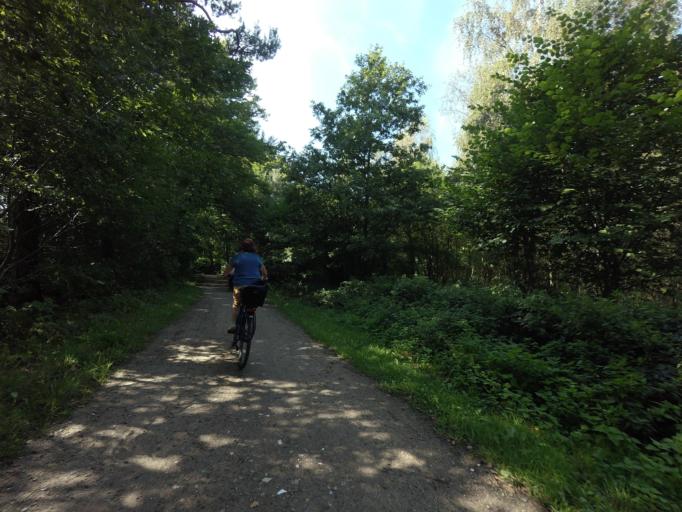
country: NL
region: Overijssel
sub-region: Gemeente Enschede
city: Enschede
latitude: 52.1857
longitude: 6.8690
